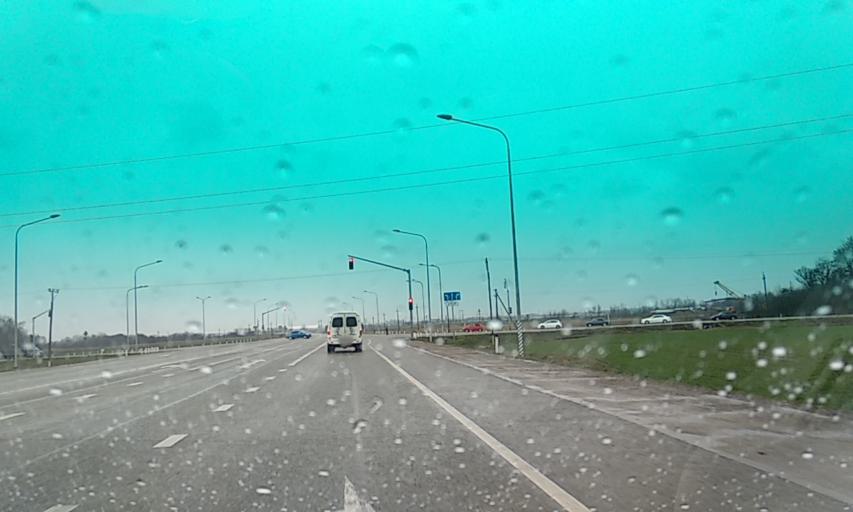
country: RU
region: Krasnodarskiy
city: Belorechensk
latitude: 44.8139
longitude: 39.8551
